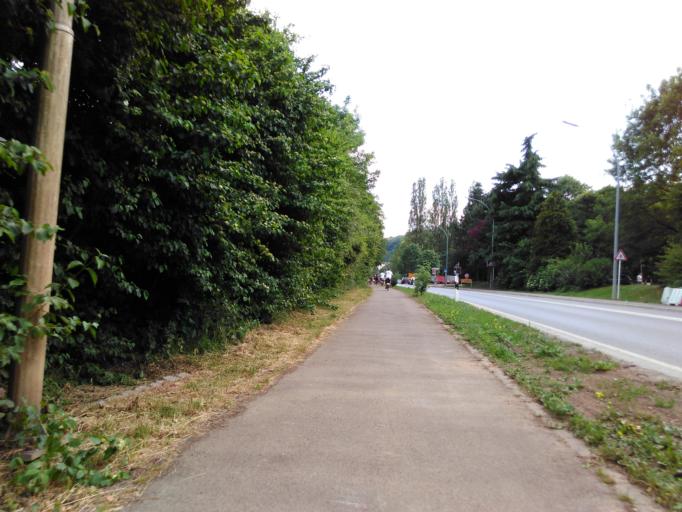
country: LU
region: Luxembourg
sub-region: Canton d'Esch-sur-Alzette
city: Schifflange
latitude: 49.5119
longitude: 6.0121
